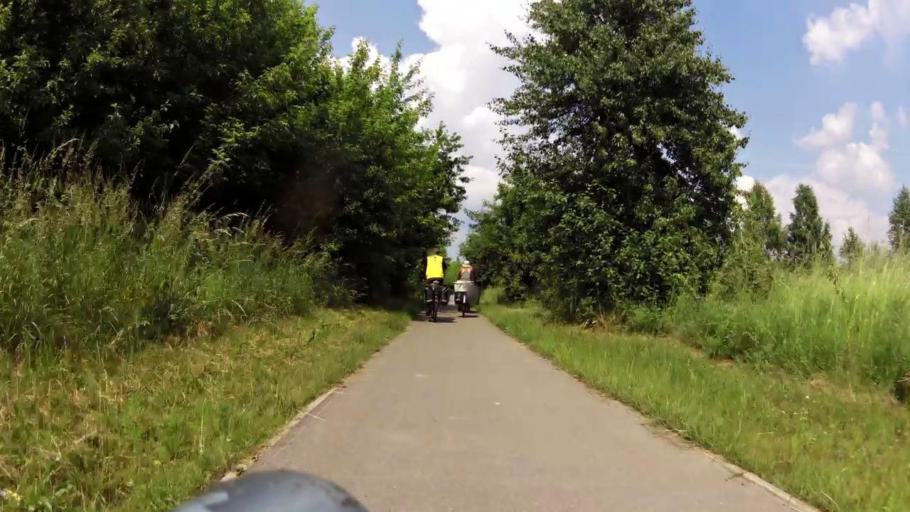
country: PL
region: Kujawsko-Pomorskie
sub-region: Powiat bydgoski
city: Koronowo
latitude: 53.2901
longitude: 17.9466
